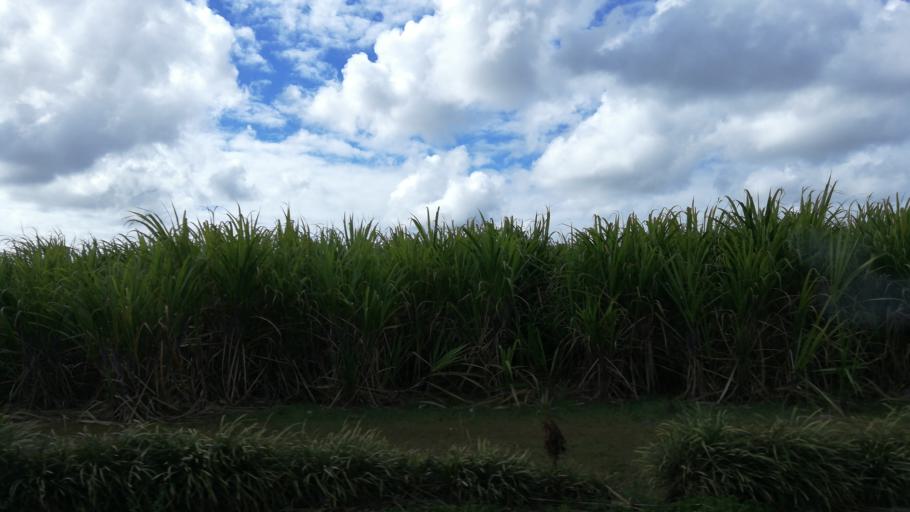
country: MU
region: Flacq
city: Camp de Masque
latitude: -20.2176
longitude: 57.6744
